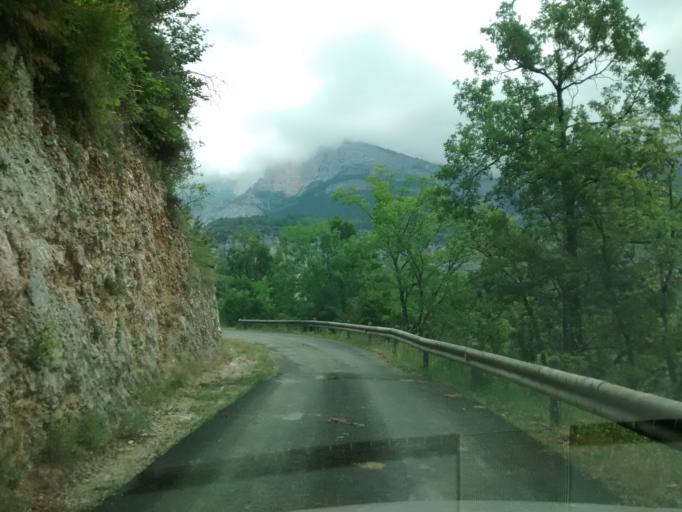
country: ES
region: Aragon
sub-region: Provincia de Huesca
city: Puertolas
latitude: 42.5930
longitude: 0.1276
